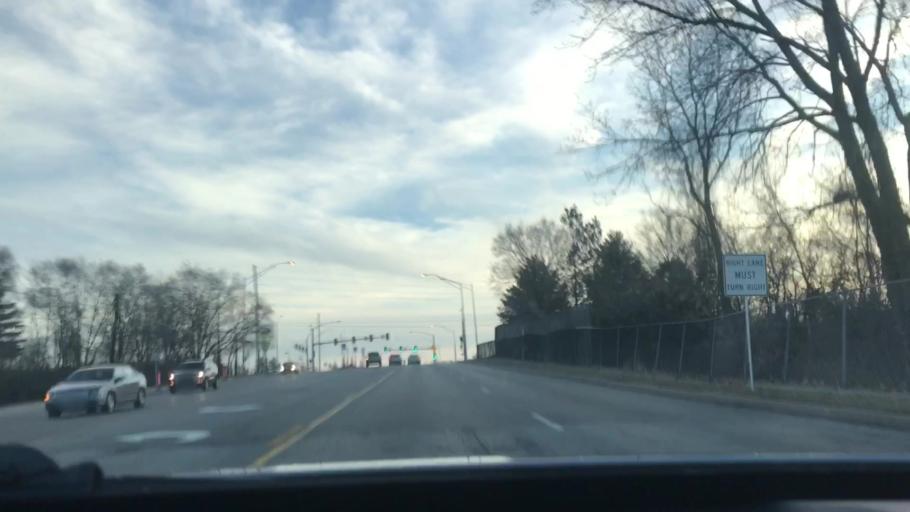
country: US
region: Missouri
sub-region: Jackson County
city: Independence
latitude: 39.0359
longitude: -94.3880
